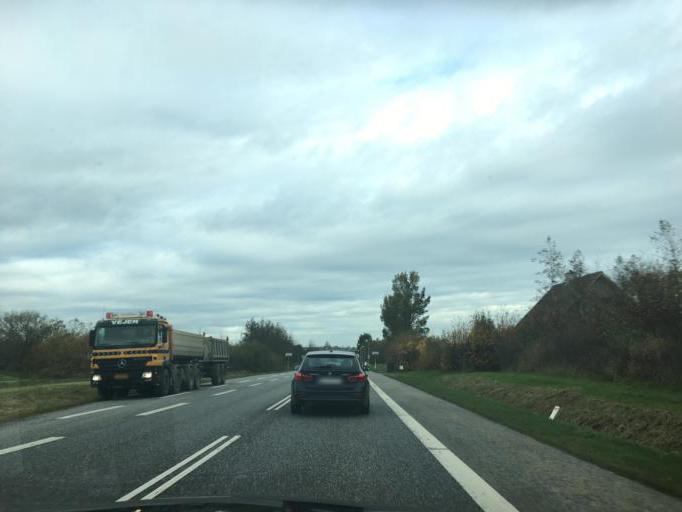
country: DK
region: South Denmark
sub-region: Vejle Kommune
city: Vejle
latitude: 55.6523
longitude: 9.5036
